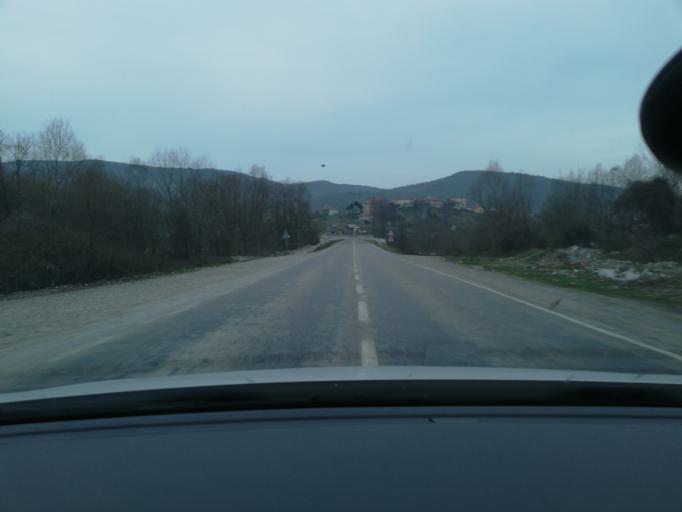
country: TR
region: Zonguldak
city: Saltukova
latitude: 41.5215
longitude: 32.0877
